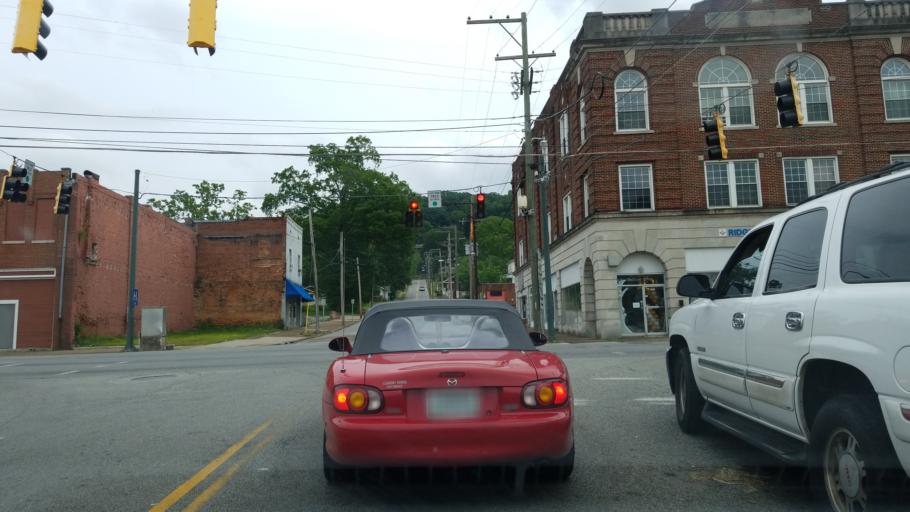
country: US
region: Tennessee
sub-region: Hamilton County
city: East Ridge
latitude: 35.0222
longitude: -85.2698
